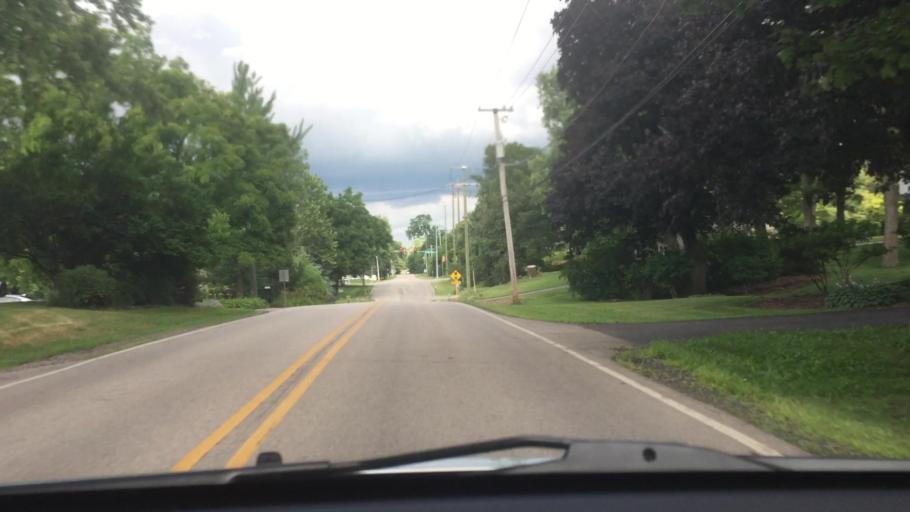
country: US
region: Illinois
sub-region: McHenry County
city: Crystal Lake
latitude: 42.2627
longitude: -88.3230
